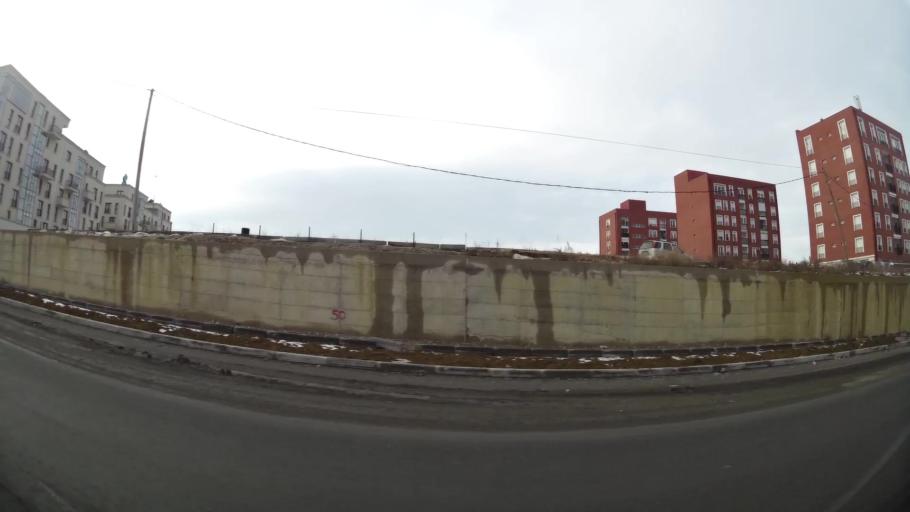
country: XK
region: Pristina
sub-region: Komuna e Prishtines
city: Pristina
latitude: 42.6354
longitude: 21.1522
